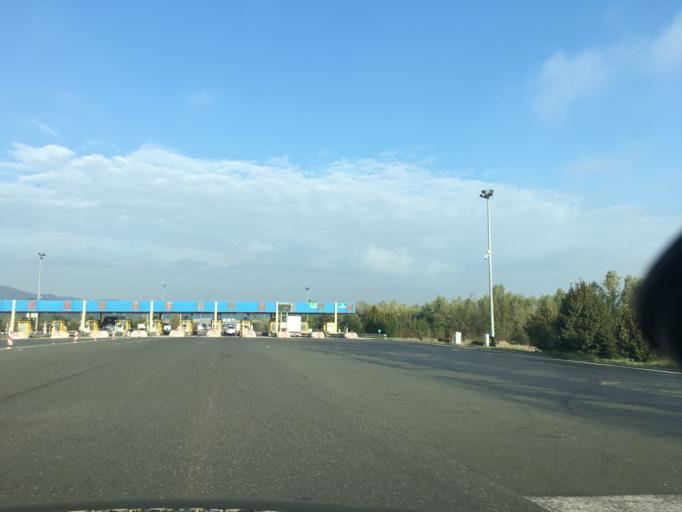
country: HR
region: Zagrebacka
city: Bregana
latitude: 45.8386
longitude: 15.7059
